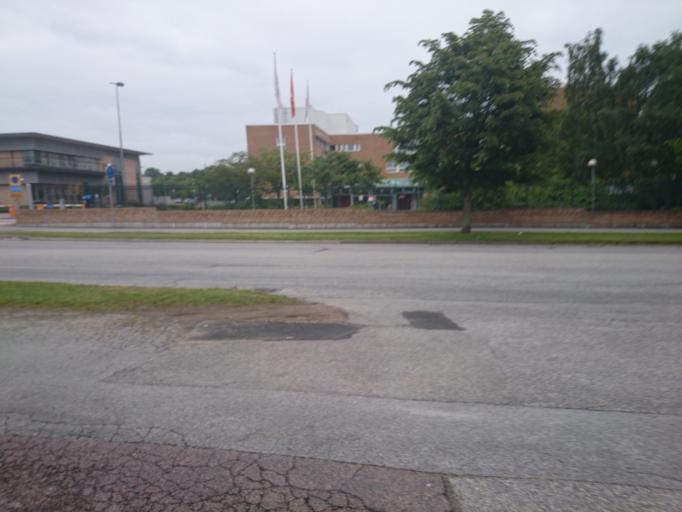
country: SE
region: Skane
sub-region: Lunds Kommun
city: Lund
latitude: 55.7100
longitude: 13.2183
